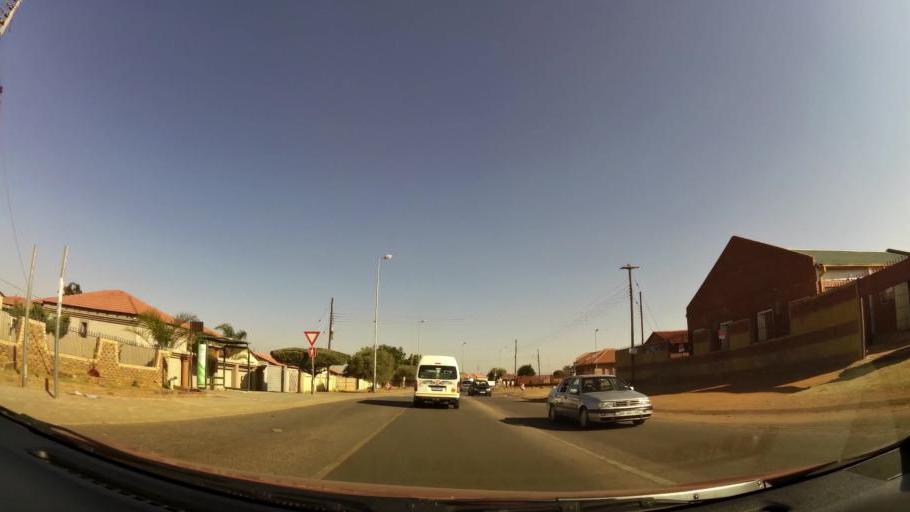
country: ZA
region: Gauteng
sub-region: City of Tshwane Metropolitan Municipality
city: Mabopane
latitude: -25.5409
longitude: 28.1047
